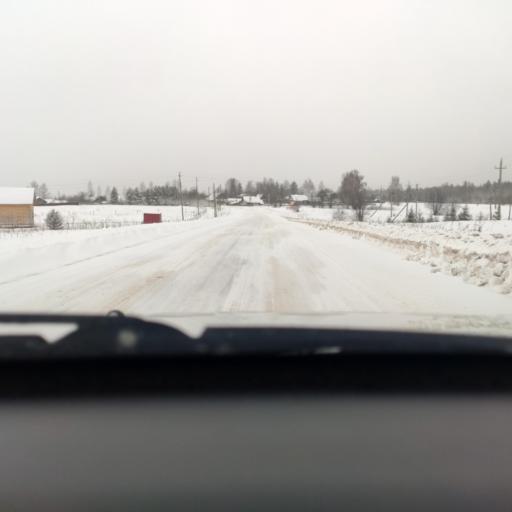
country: RU
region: Perm
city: Novyye Lyady
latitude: 58.1823
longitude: 56.5505
